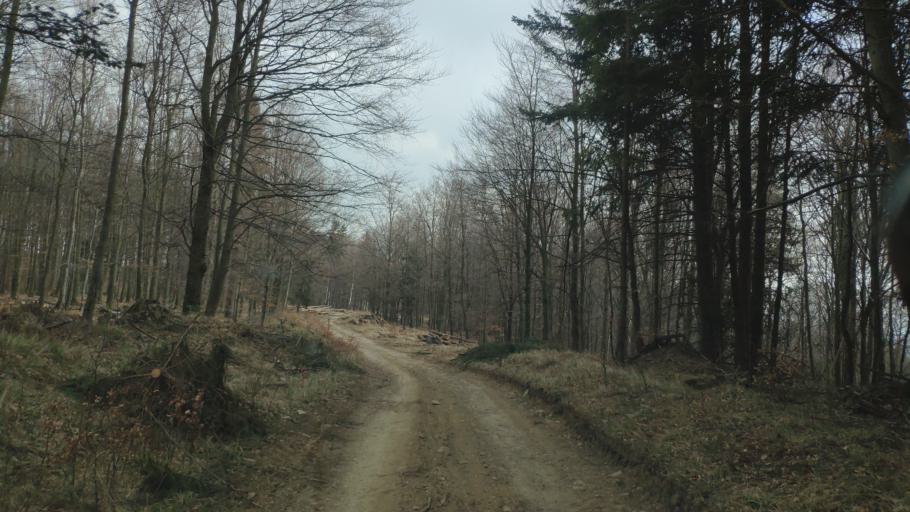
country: SK
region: Kosicky
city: Moldava nad Bodvou
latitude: 48.7435
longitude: 21.0433
